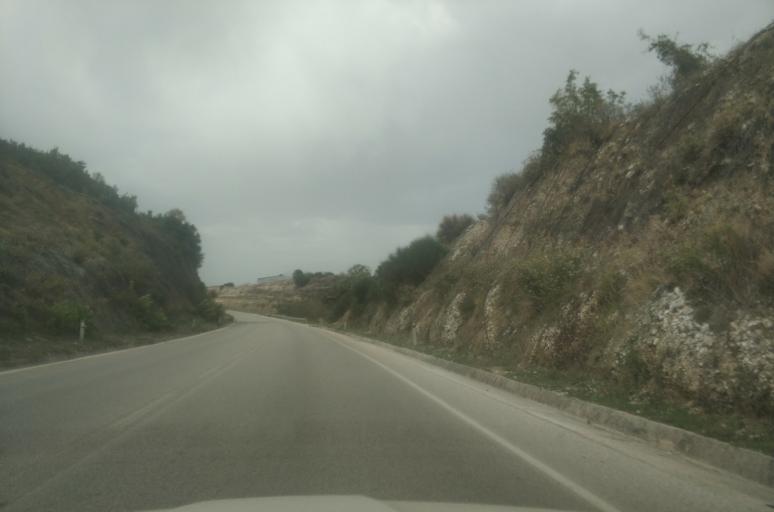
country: AL
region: Gjirokaster
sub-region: Rrethi i Tepelenes
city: Tepelene
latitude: 40.2656
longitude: 20.0506
